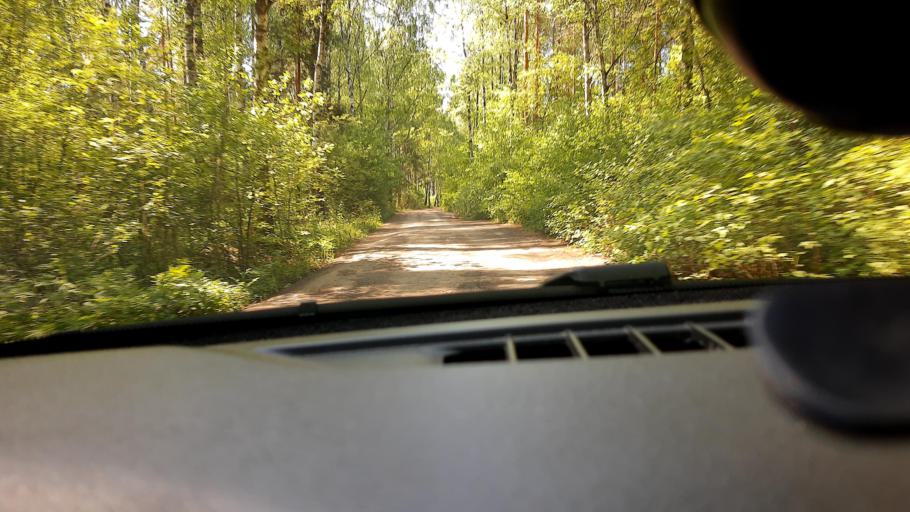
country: RU
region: Nizjnij Novgorod
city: Gorbatovka
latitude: 56.2859
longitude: 43.8038
